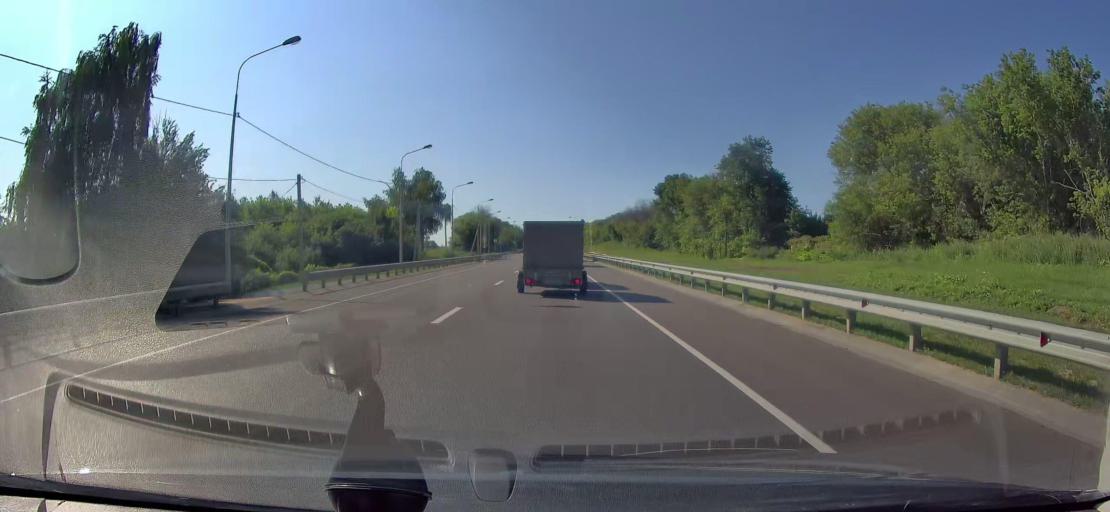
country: RU
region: Orjol
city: Kromy
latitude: 52.6191
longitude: 35.7600
